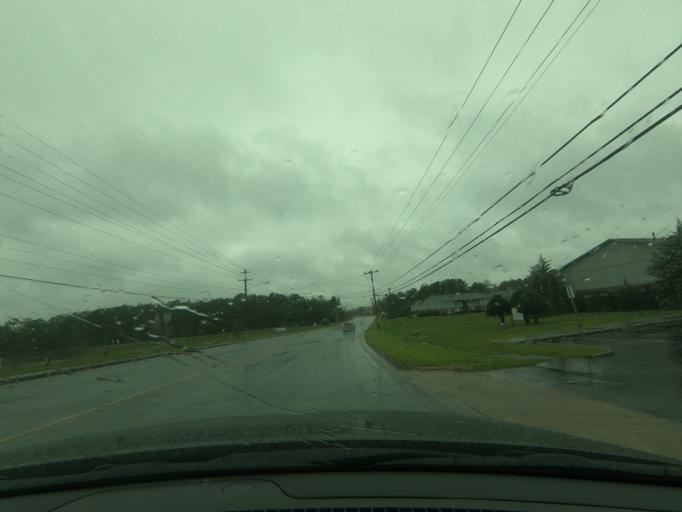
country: US
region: Georgia
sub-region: Gordon County
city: Calhoun
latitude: 34.5120
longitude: -84.9264
